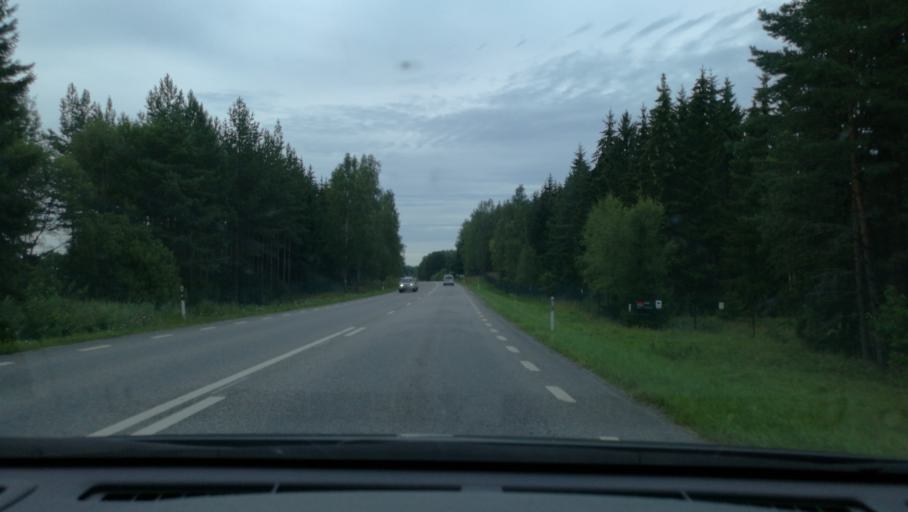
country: SE
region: Soedermanland
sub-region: Katrineholms Kommun
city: Katrineholm
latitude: 59.0108
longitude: 16.2127
